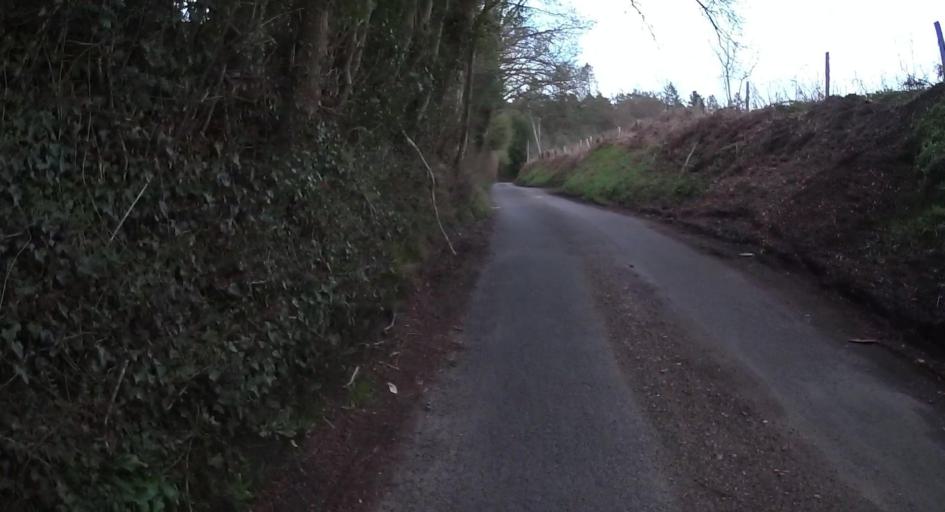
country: GB
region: England
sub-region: Hampshire
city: Lindford
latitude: 51.1412
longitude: -0.8226
